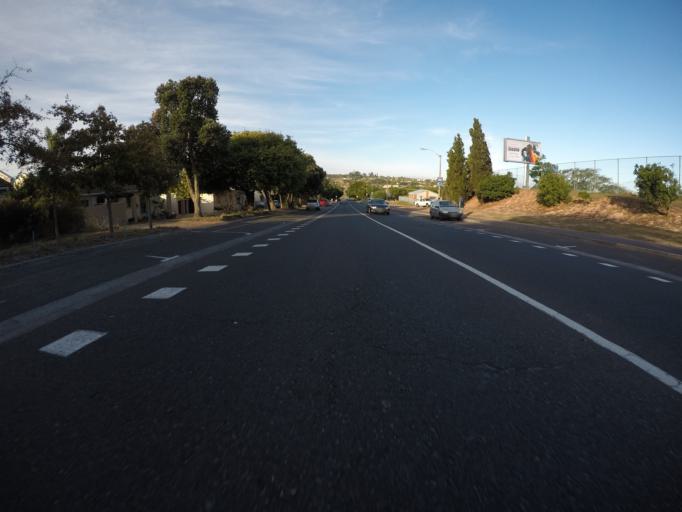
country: ZA
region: Western Cape
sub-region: City of Cape Town
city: Kraaifontein
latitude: -33.8625
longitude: 18.6627
